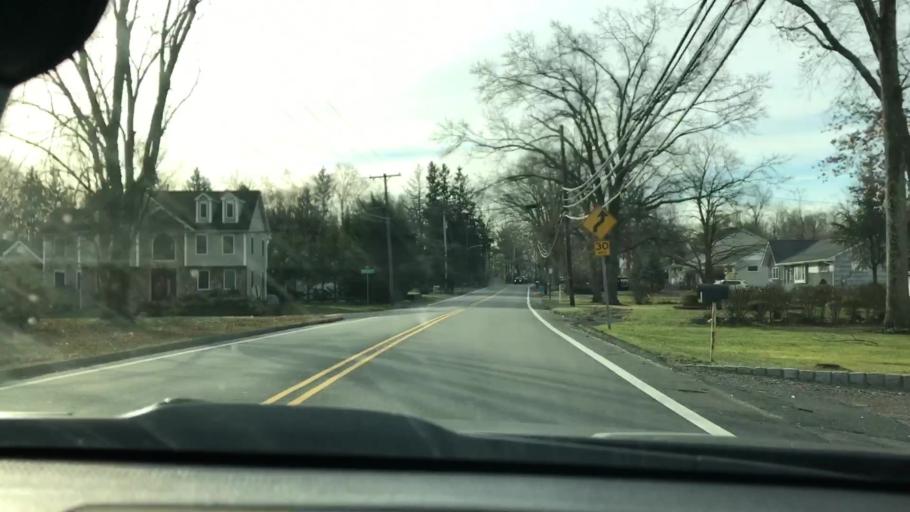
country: US
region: New Jersey
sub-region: Morris County
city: Parsippany
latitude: 40.8382
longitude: -74.4214
